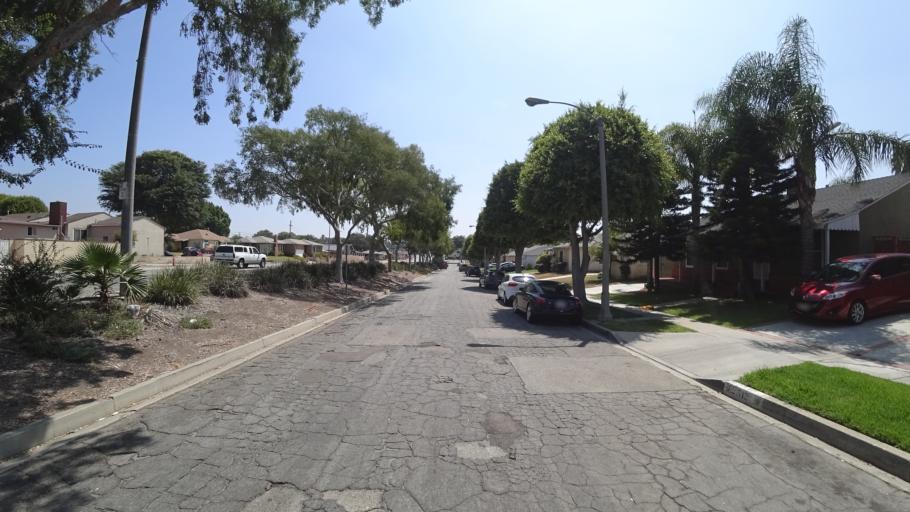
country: US
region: California
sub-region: Los Angeles County
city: Westmont
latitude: 33.9453
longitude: -118.3217
